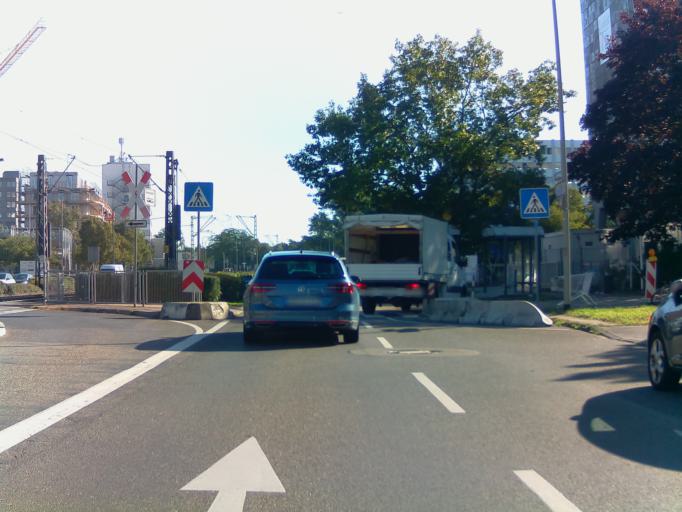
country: DE
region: Hesse
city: Niederrad
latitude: 50.0780
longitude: 8.6285
